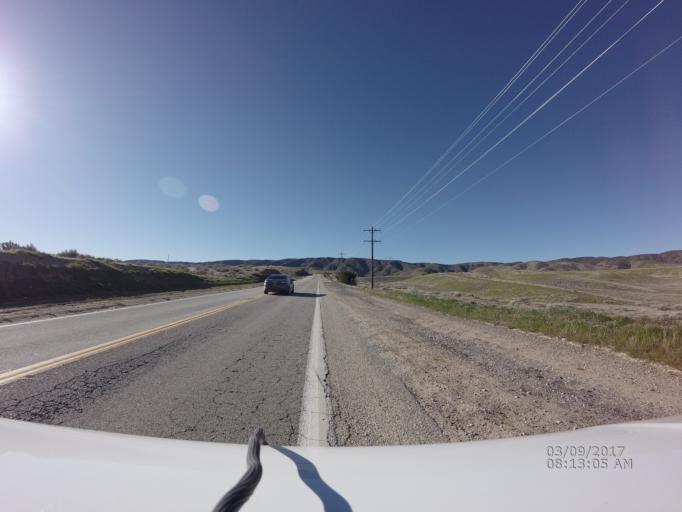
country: US
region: California
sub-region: Los Angeles County
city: Leona Valley
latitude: 34.6729
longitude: -118.3242
